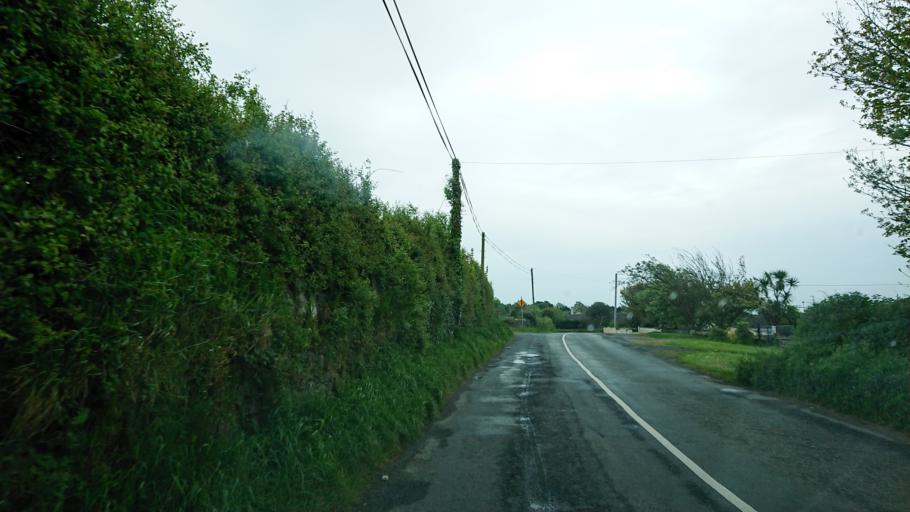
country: IE
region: Munster
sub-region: Waterford
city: Waterford
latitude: 52.2266
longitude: -7.0579
